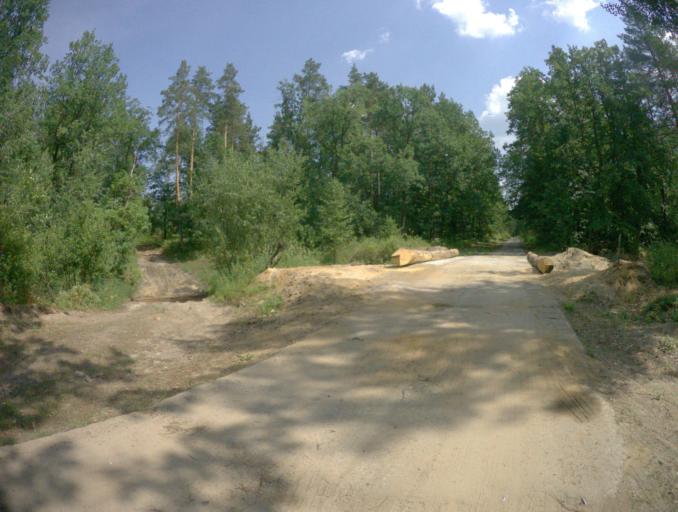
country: RU
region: Nizjnij Novgorod
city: Frolishchi
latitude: 56.4029
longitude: 42.5818
